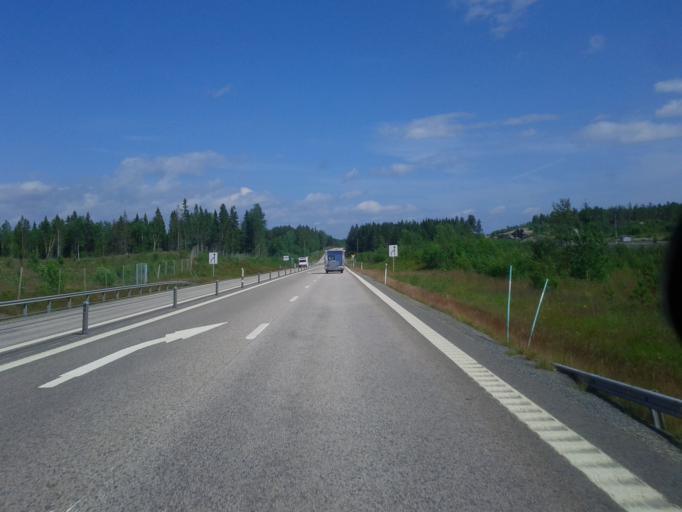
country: SE
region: Vaesterbotten
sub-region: Nordmalings Kommun
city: Nordmaling
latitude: 63.5090
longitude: 19.3533
